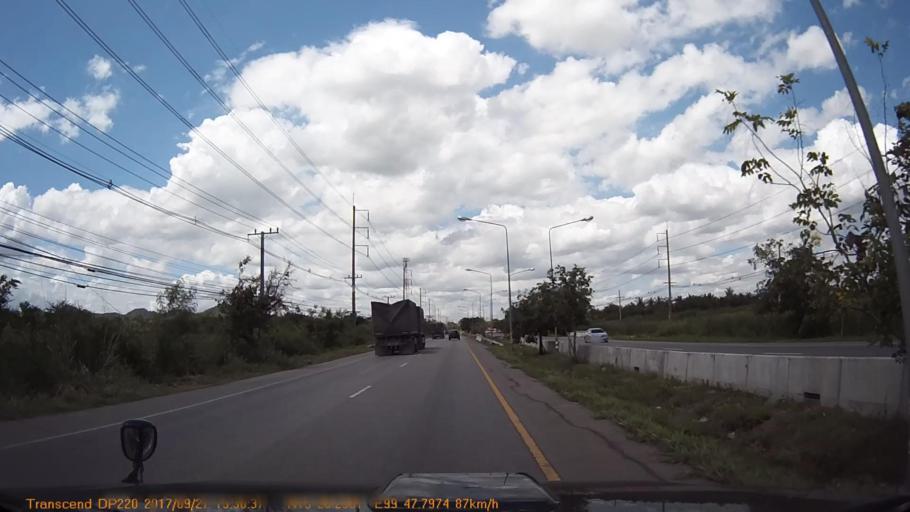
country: TH
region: Ratchaburi
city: Ratchaburi
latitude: 13.4708
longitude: 99.7966
